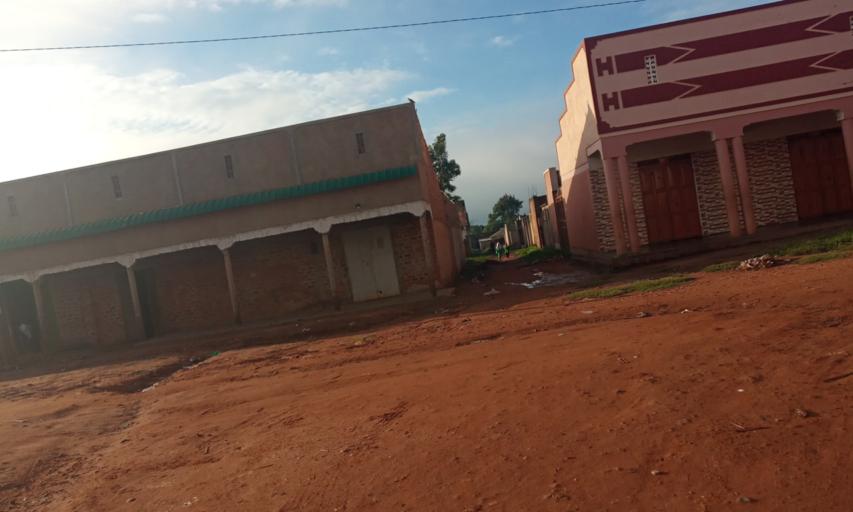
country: UG
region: Eastern Region
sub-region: Mbale District
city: Mbale
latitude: 1.1408
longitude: 34.1652
